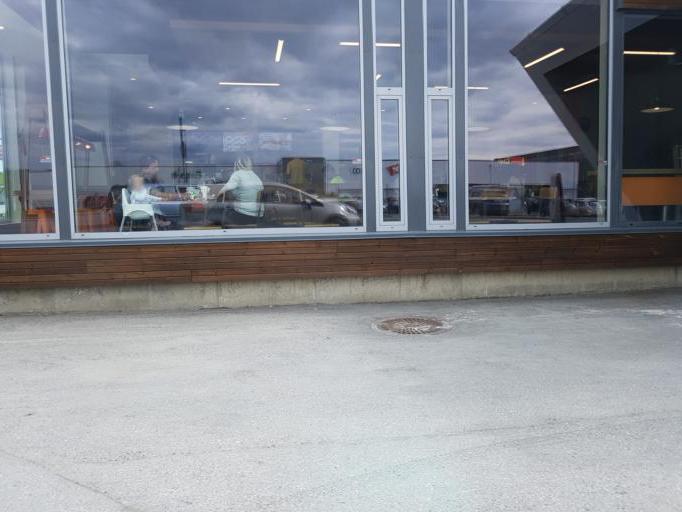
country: NO
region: Nord-Trondelag
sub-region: Levanger
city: Levanger
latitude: 63.7338
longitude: 11.2835
